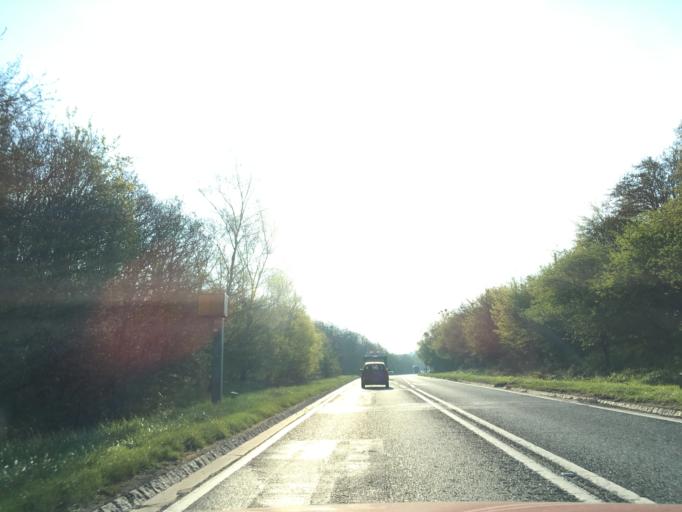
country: GB
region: England
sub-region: Oxfordshire
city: Eynsham
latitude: 51.7908
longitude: -1.4111
